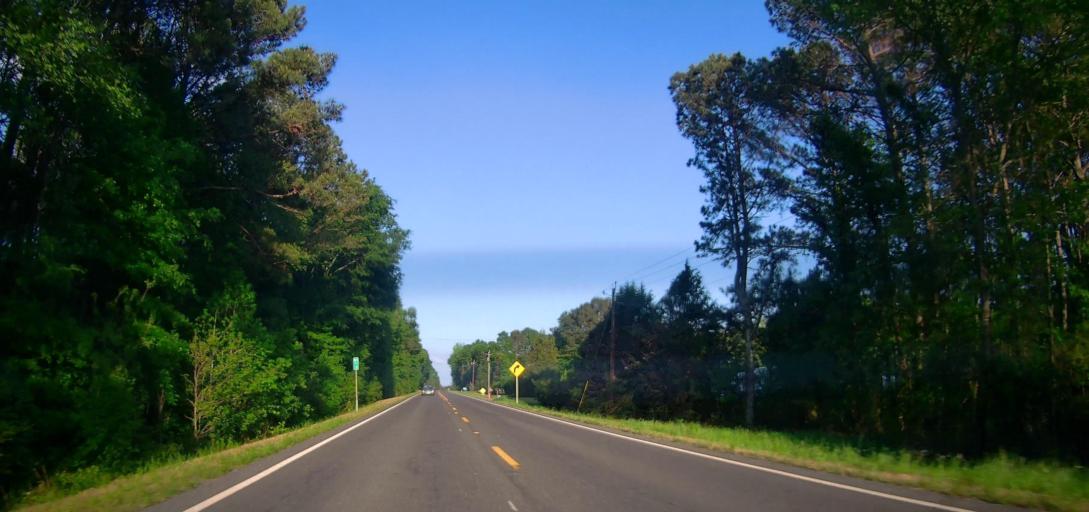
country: US
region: Georgia
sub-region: Walton County
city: Social Circle
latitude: 33.5089
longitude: -83.6736
